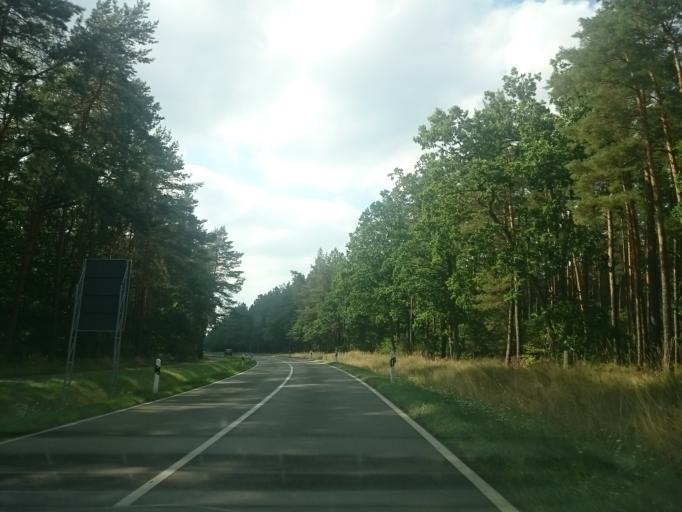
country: DE
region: Mecklenburg-Vorpommern
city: Torgelow
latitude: 53.6338
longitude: 13.9854
